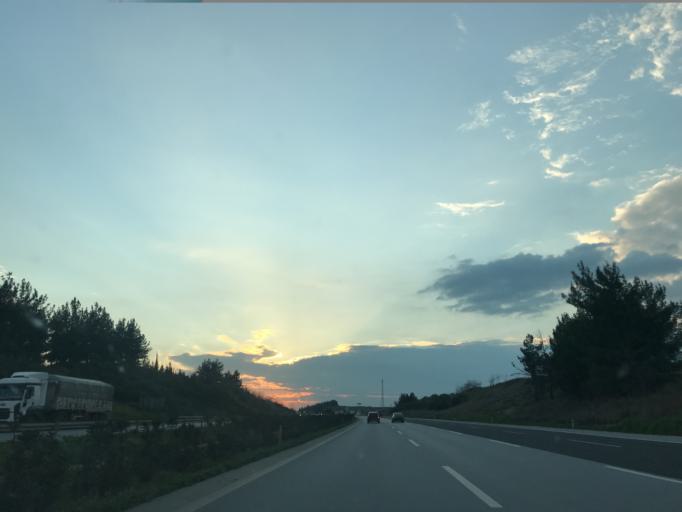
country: TR
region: Mersin
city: Yenice
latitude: 37.0199
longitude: 35.0170
